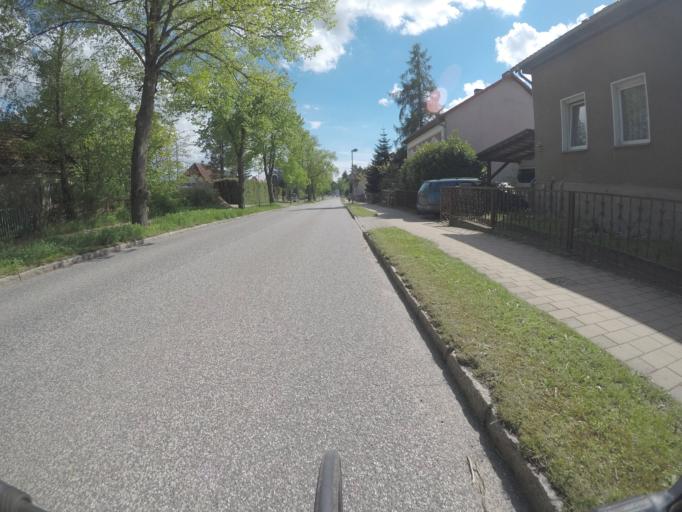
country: DE
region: Brandenburg
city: Bernau bei Berlin
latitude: 52.6987
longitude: 13.5883
